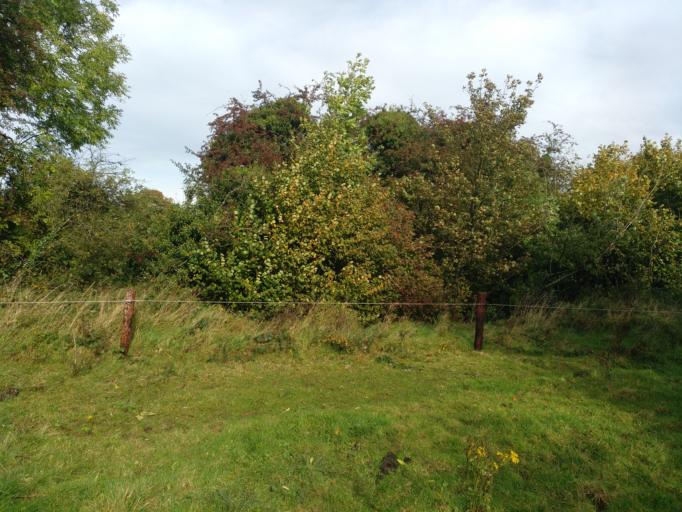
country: IE
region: Leinster
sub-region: Kilkenny
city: Castlecomer
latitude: 52.7889
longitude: -7.2066
